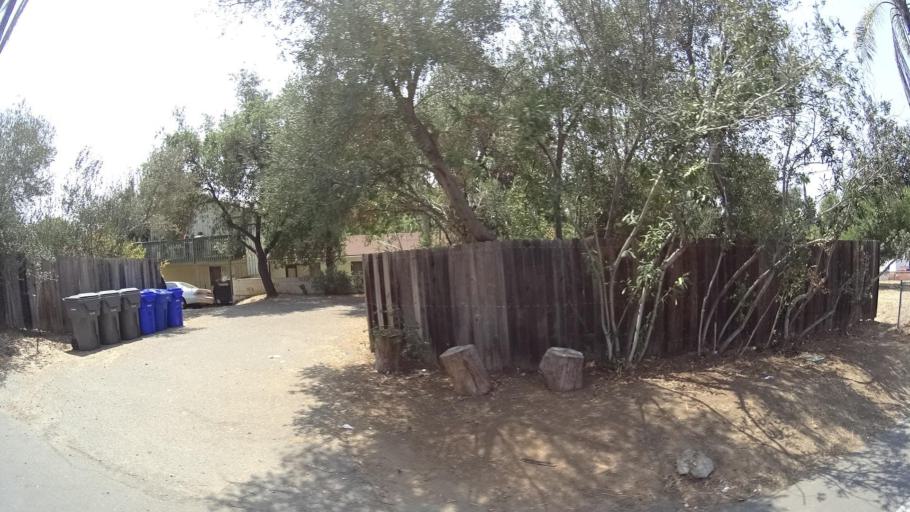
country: US
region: California
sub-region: San Diego County
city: Fallbrook
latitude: 33.3875
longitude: -117.2359
